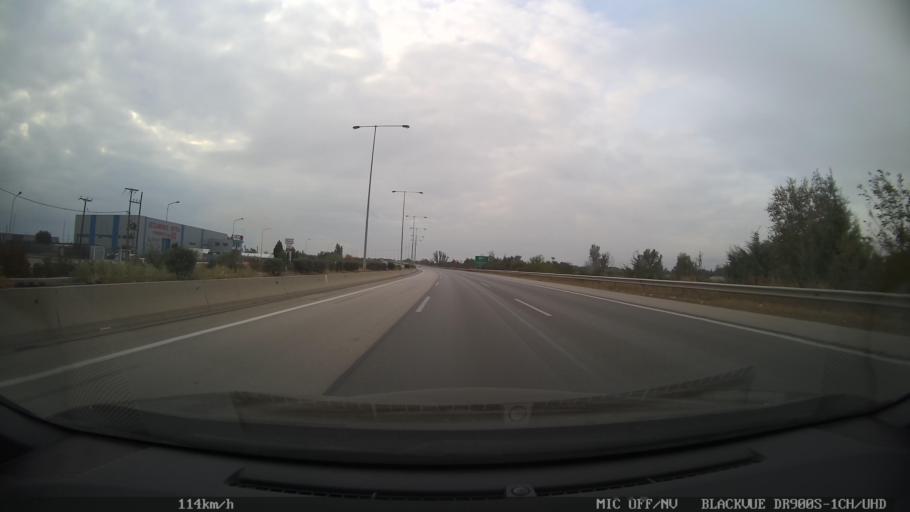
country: GR
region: Central Macedonia
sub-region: Nomos Thessalonikis
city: Nea Magnisia
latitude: 40.6759
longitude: 22.8323
